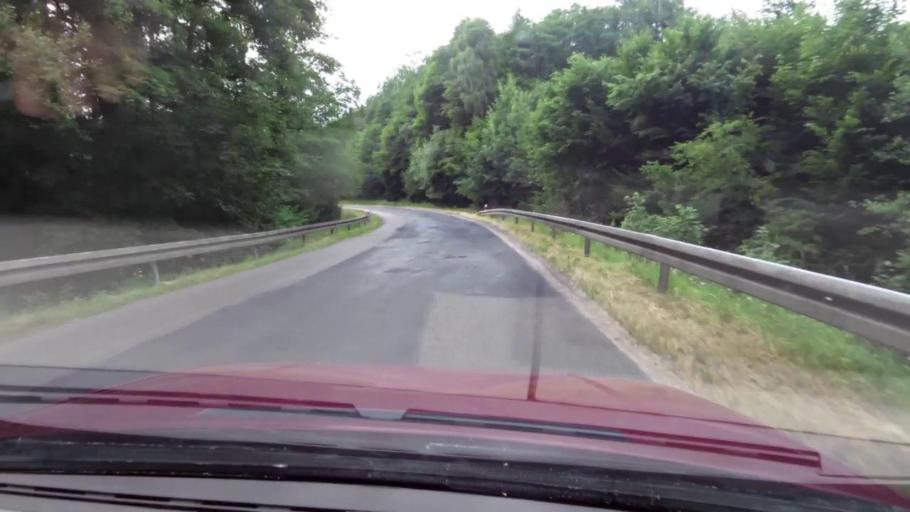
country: PL
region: Pomeranian Voivodeship
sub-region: Powiat bytowski
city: Trzebielino
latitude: 54.2695
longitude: 17.0232
